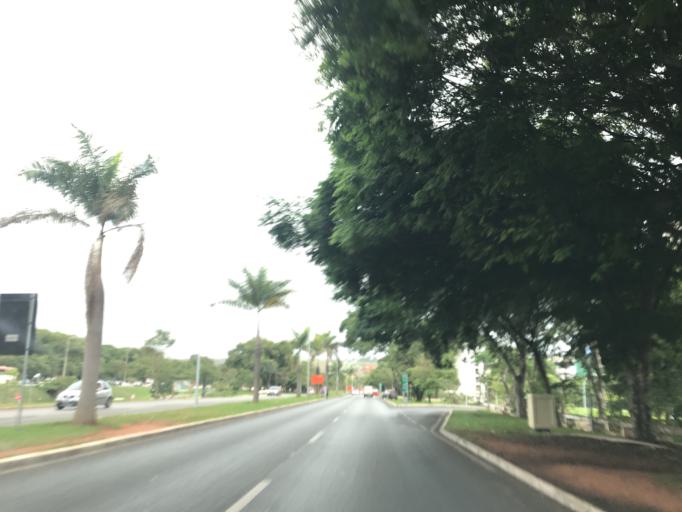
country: BR
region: Federal District
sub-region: Brasilia
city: Brasilia
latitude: -15.7405
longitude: -47.8903
